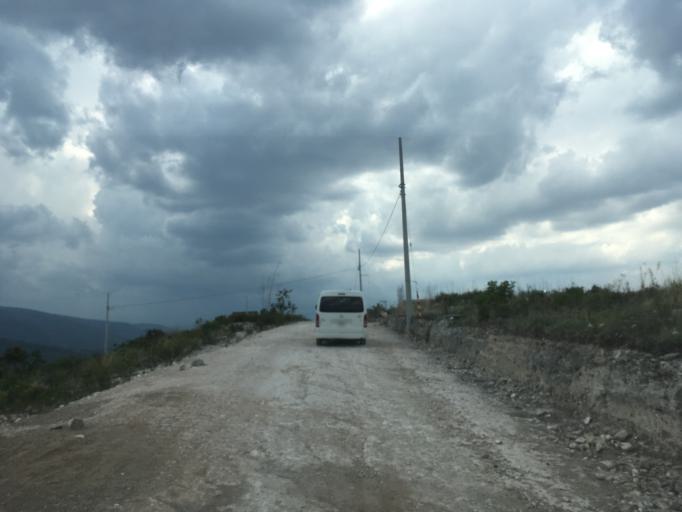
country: MX
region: Oaxaca
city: Santiago Tilantongo
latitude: 17.2238
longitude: -97.2729
